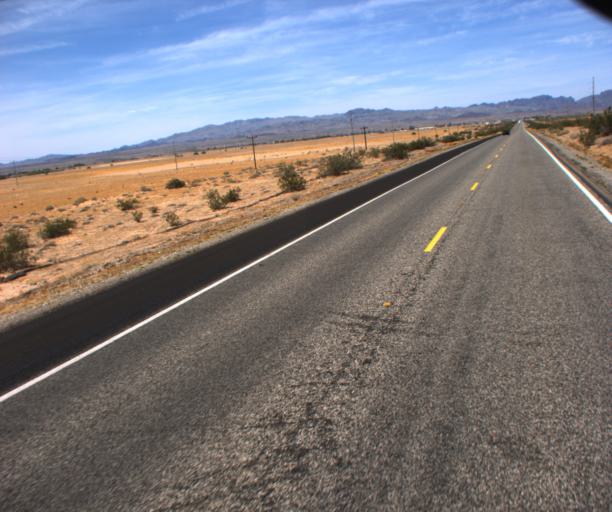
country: US
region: Arizona
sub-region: La Paz County
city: Parker
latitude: 34.1047
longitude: -114.2776
